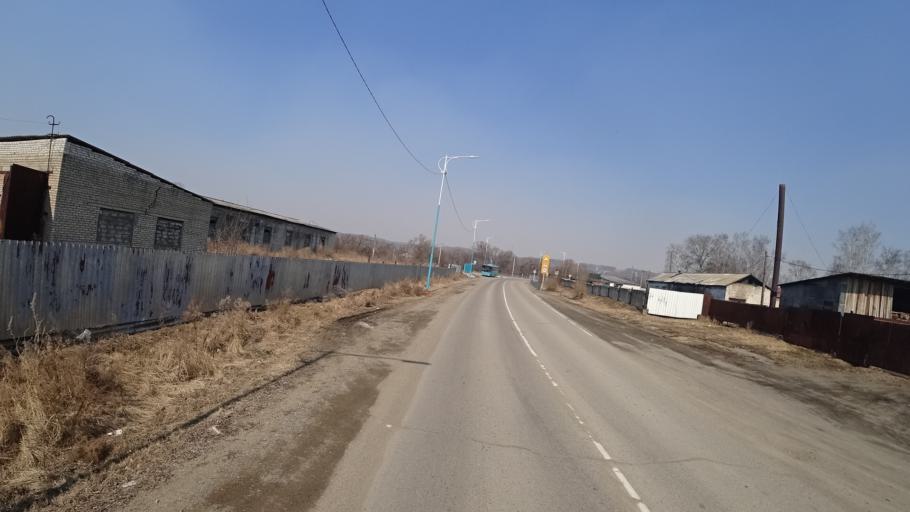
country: RU
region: Amur
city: Novobureyskiy
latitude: 49.7916
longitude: 129.9050
